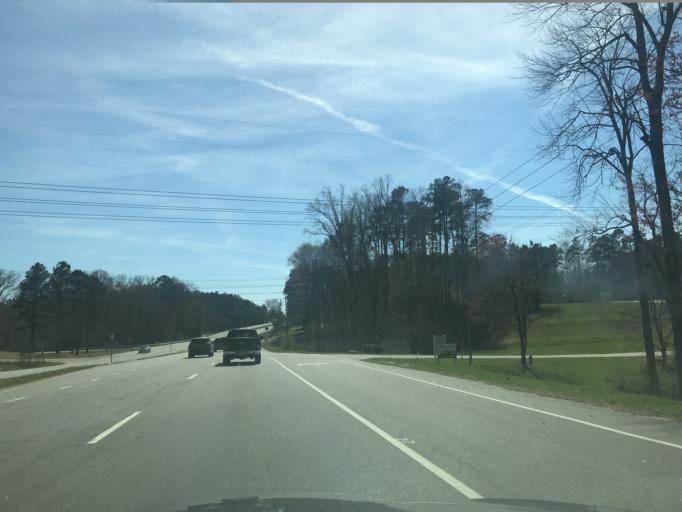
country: US
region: North Carolina
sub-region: Wake County
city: Fuquay-Varina
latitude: 35.6458
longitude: -78.7094
